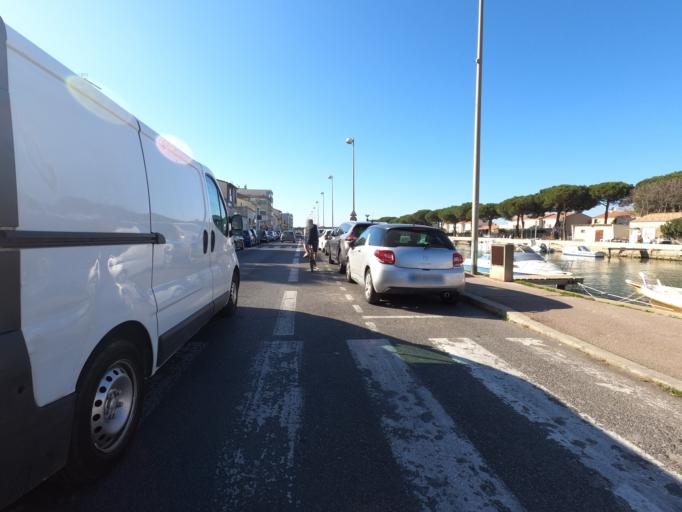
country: FR
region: Languedoc-Roussillon
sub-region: Departement de l'Herault
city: Palavas-les-Flots
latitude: 43.5290
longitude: 3.9278
